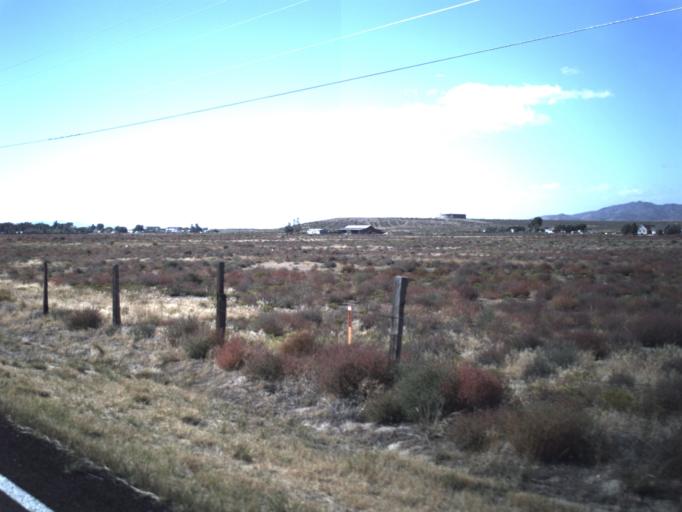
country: US
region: Utah
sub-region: Beaver County
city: Milford
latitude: 38.4137
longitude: -113.0099
